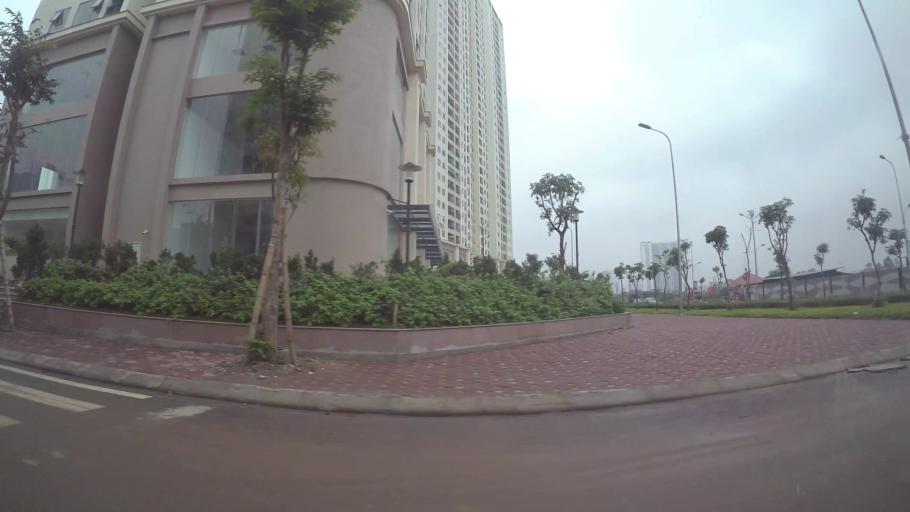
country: VN
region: Ha Noi
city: Van Dien
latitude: 20.9749
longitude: 105.8703
